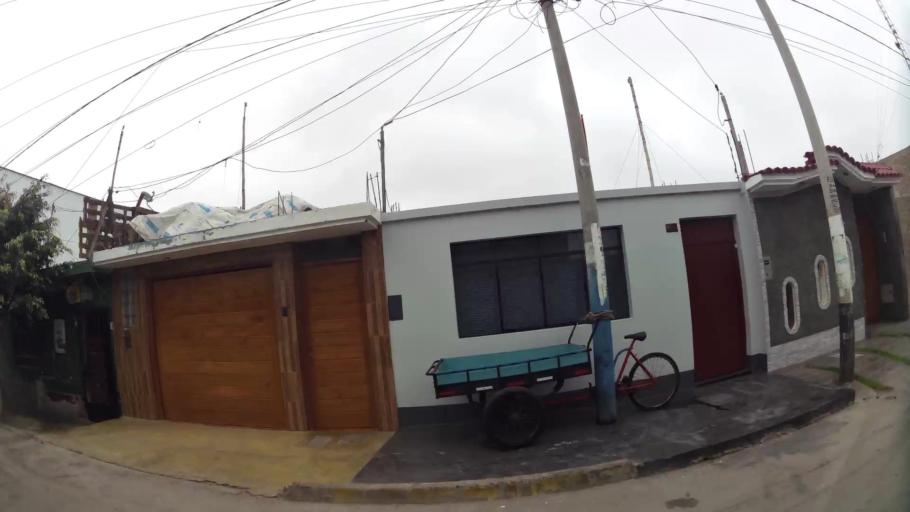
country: PE
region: Ica
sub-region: Provincia de Pisco
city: Pisco
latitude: -13.7289
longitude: -76.2214
